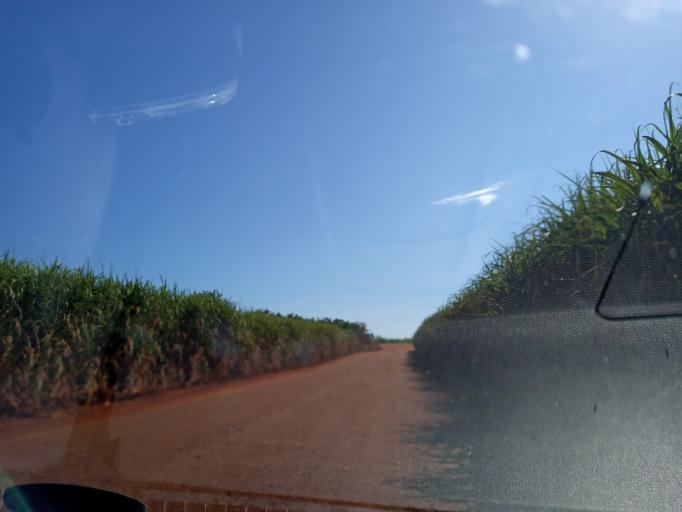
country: BR
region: Goias
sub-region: Itumbiara
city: Itumbiara
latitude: -18.4458
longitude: -49.1759
